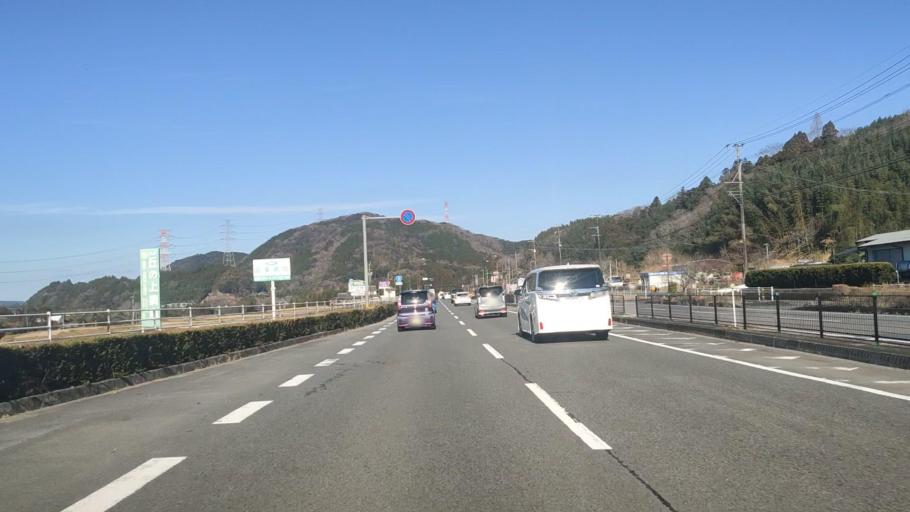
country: JP
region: Oita
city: Oita
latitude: 33.1033
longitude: 131.6527
